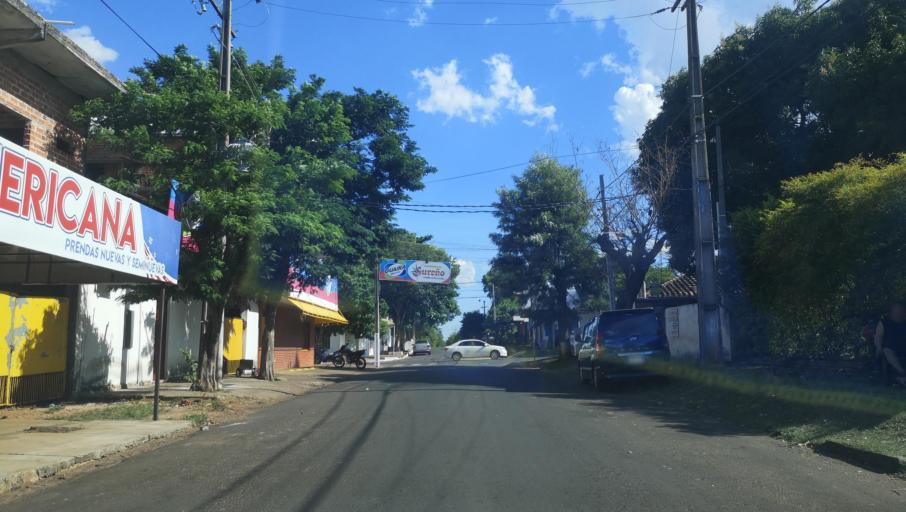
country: PY
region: Misiones
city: Santa Maria
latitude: -26.8887
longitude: -57.0203
